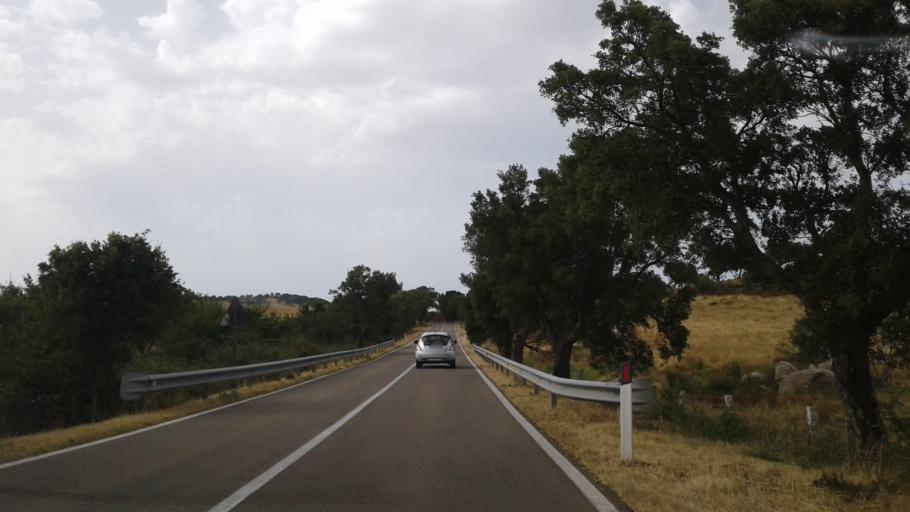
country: IT
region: Sardinia
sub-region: Provincia di Olbia-Tempio
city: Sant'Antonio di Gallura
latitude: 40.9466
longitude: 9.2982
